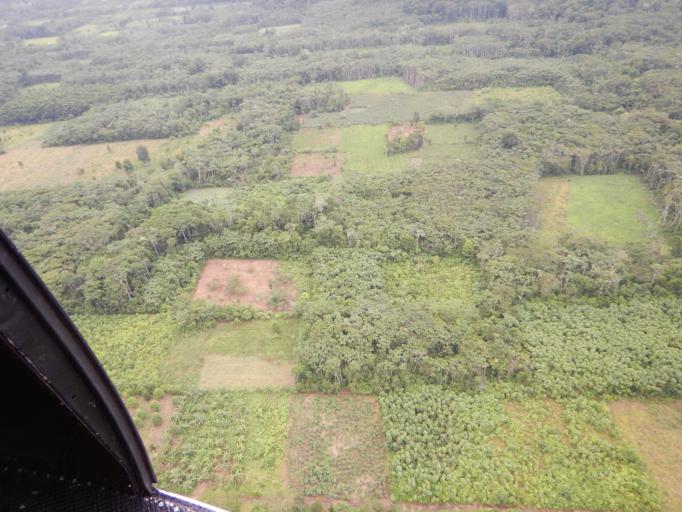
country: BO
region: Cochabamba
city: Chimore
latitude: -17.2305
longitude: -64.6138
